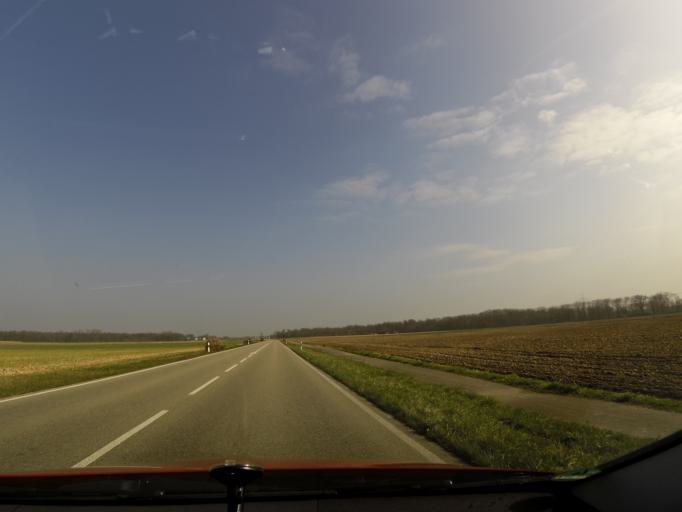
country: DE
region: Baden-Wuerttemberg
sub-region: Freiburg Region
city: Willstatt
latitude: 48.6054
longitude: 7.8824
